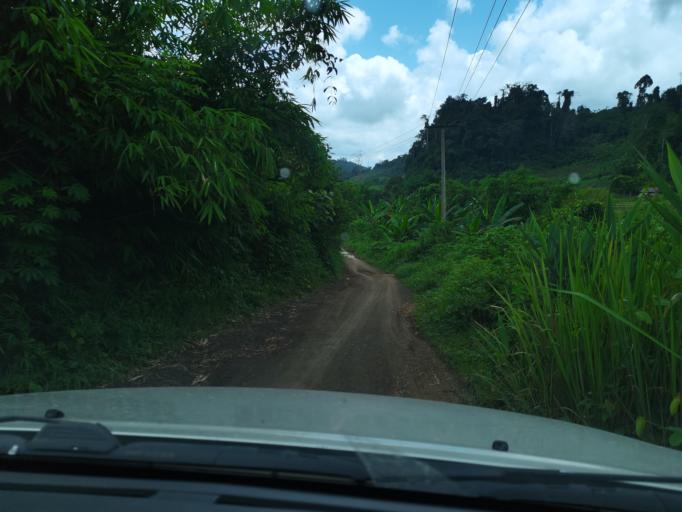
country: LA
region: Loungnamtha
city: Muang Long
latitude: 20.7595
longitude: 101.0167
